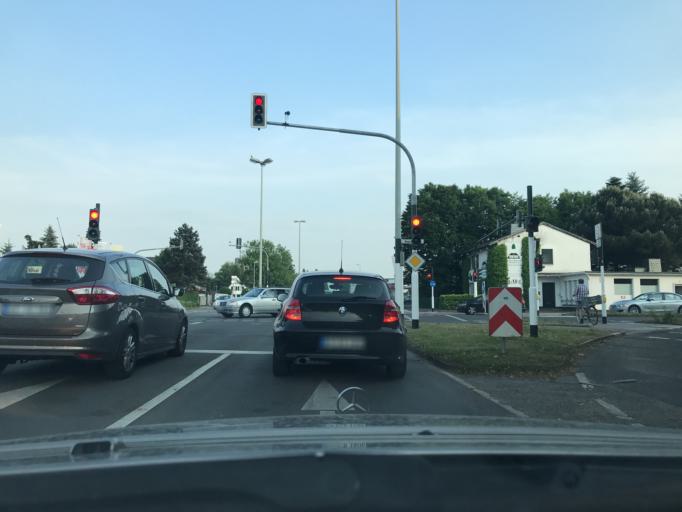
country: DE
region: North Rhine-Westphalia
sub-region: Regierungsbezirk Dusseldorf
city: Krefeld
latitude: 51.3301
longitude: 6.5890
